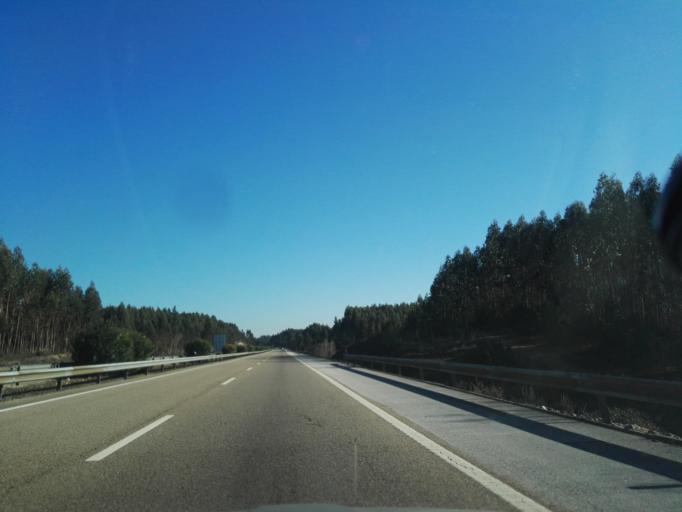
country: PT
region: Santarem
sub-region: Chamusca
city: Vila Nova da Barquinha
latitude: 39.4883
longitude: -8.4240
